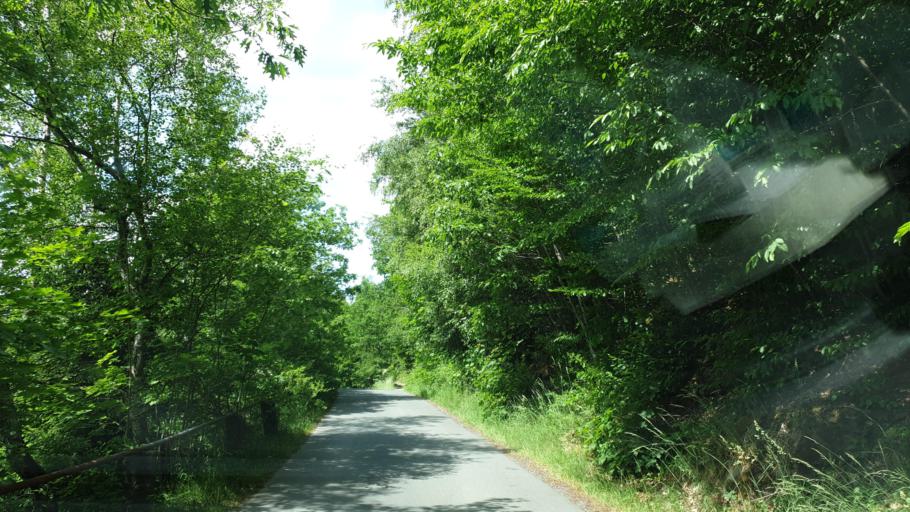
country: DE
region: Saxony
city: Adorf
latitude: 50.3263
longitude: 12.2611
